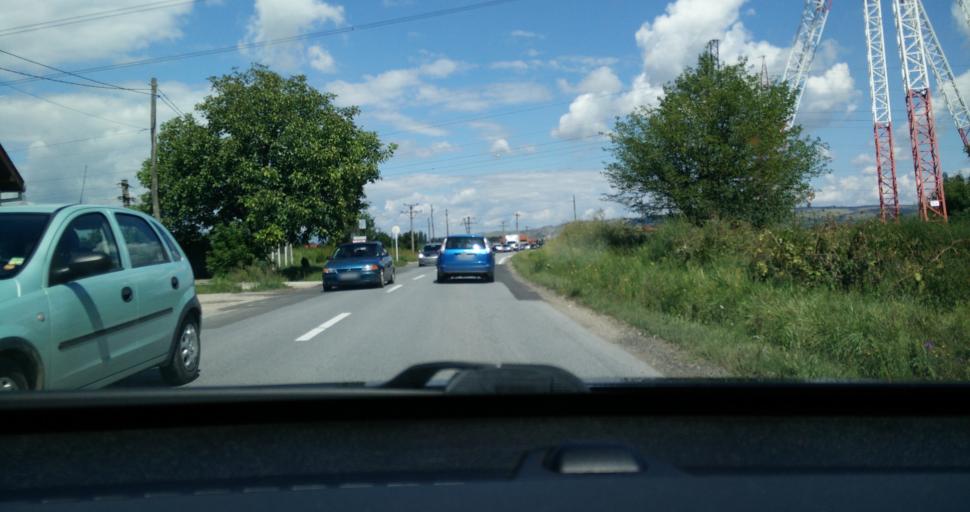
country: RO
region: Alba
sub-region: Municipiul Sebes
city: Petresti
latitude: 45.9303
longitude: 23.5604
